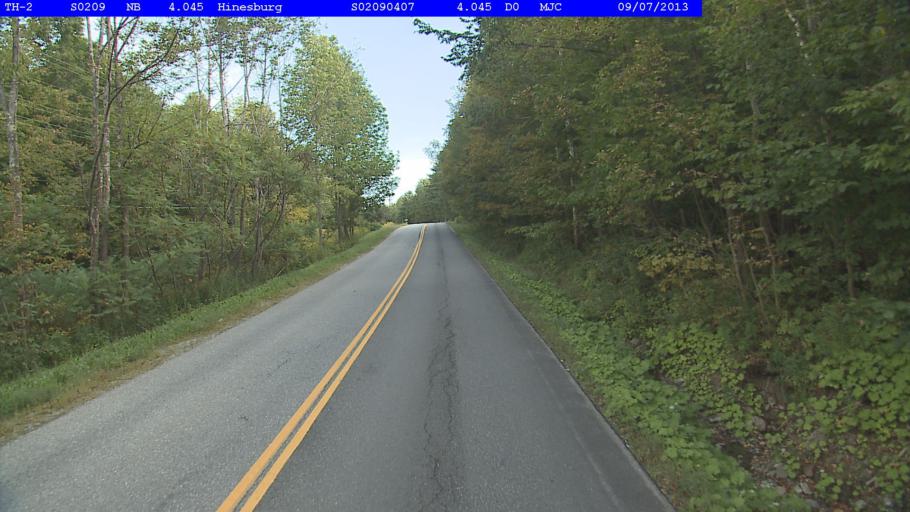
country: US
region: Vermont
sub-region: Chittenden County
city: Hinesburg
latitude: 44.3681
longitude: -73.0680
